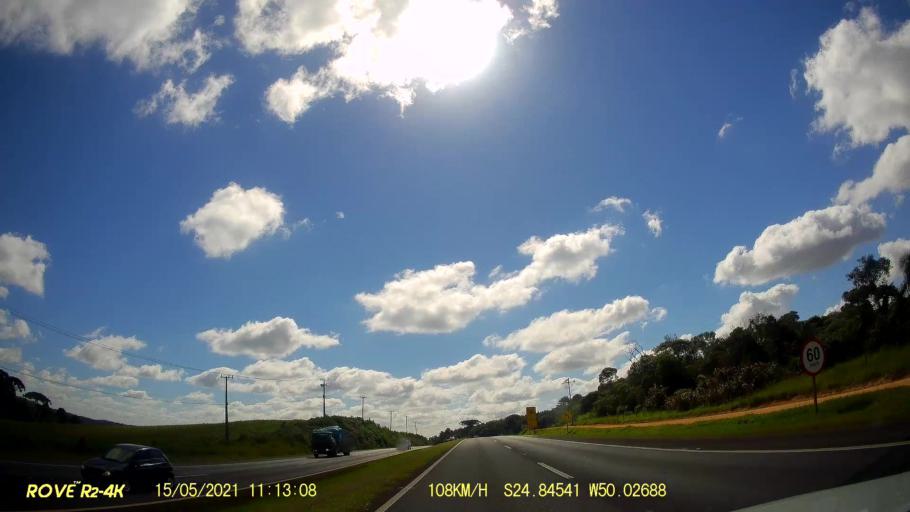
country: BR
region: Parana
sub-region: Castro
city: Castro
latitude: -24.8456
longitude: -50.0270
